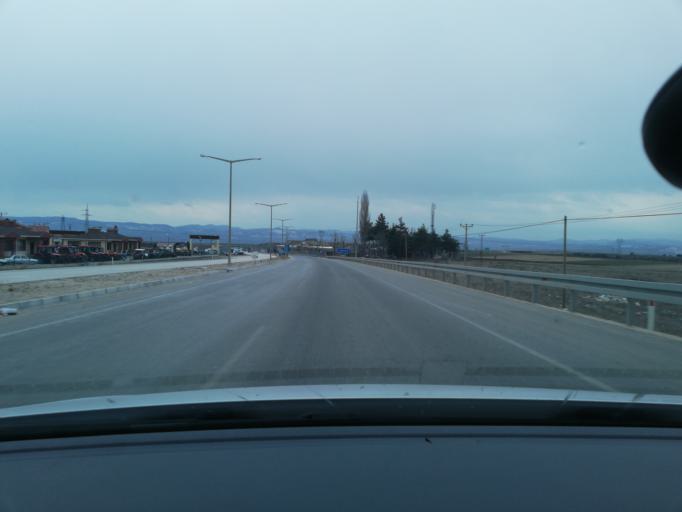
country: TR
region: Bolu
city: Gerede
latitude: 40.7855
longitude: 32.2102
